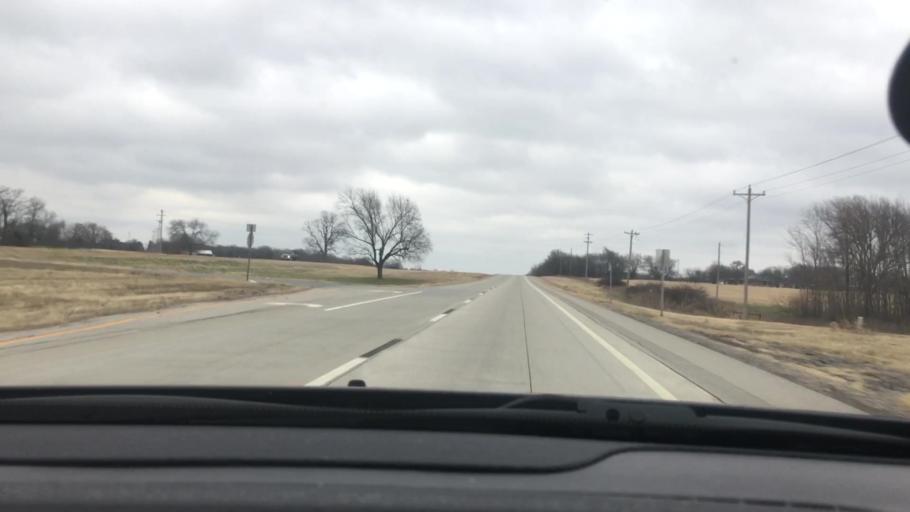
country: US
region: Oklahoma
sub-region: Bryan County
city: Durant
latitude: 34.1748
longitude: -96.2505
